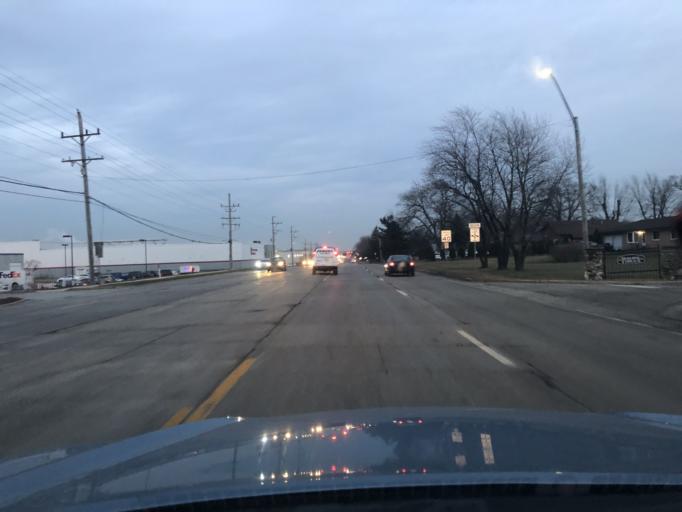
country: US
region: Illinois
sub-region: Cook County
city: Elk Grove Village
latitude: 41.9929
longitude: -87.9692
